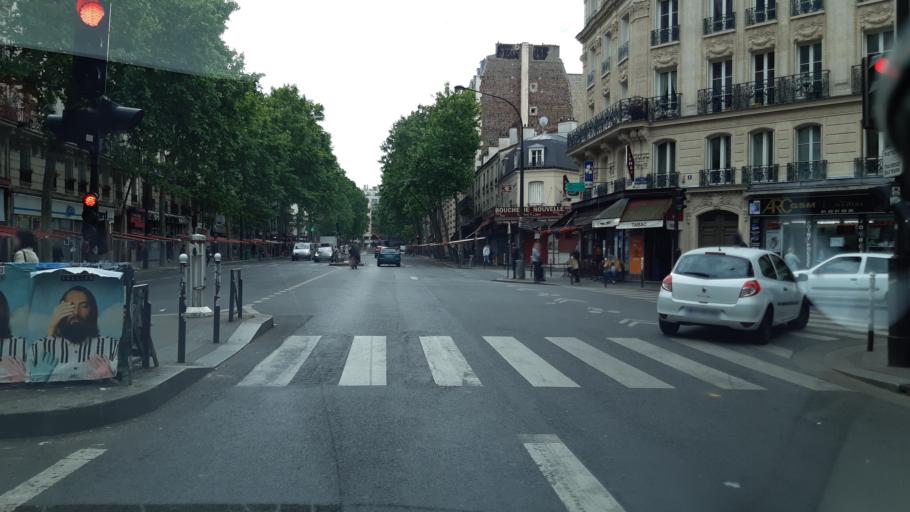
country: FR
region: Ile-de-France
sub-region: Paris
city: Saint-Ouen
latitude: 48.8940
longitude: 2.3476
